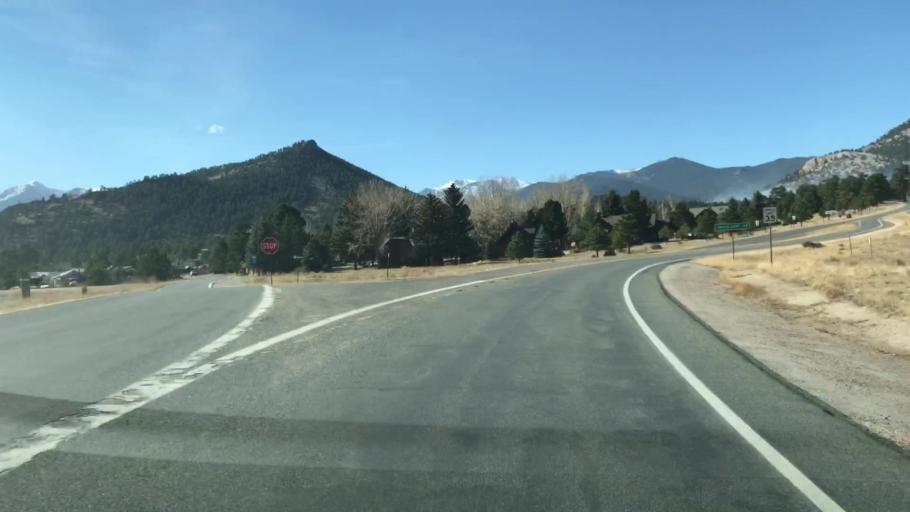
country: US
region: Colorado
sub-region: Larimer County
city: Estes Park
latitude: 40.3636
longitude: -105.5487
